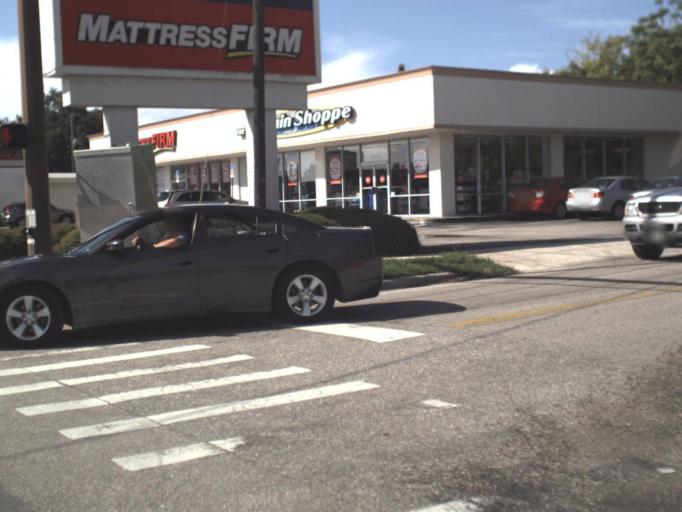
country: US
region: Florida
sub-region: Sarasota County
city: South Sarasota
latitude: 27.2953
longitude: -82.5307
